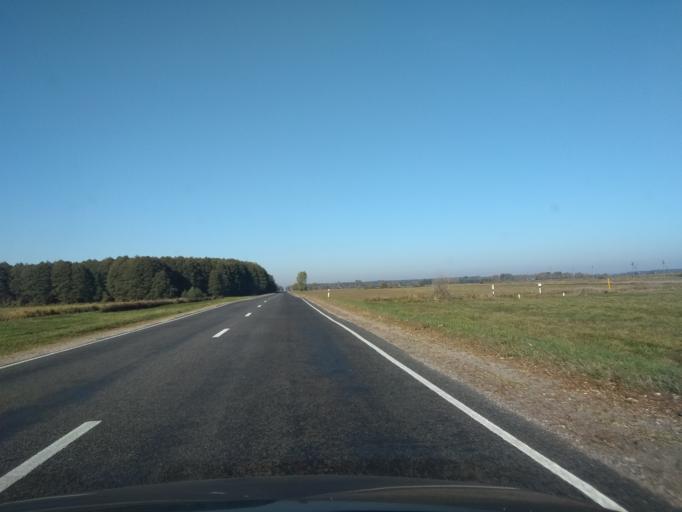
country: BY
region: Brest
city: Malaryta
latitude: 51.9419
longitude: 24.0314
